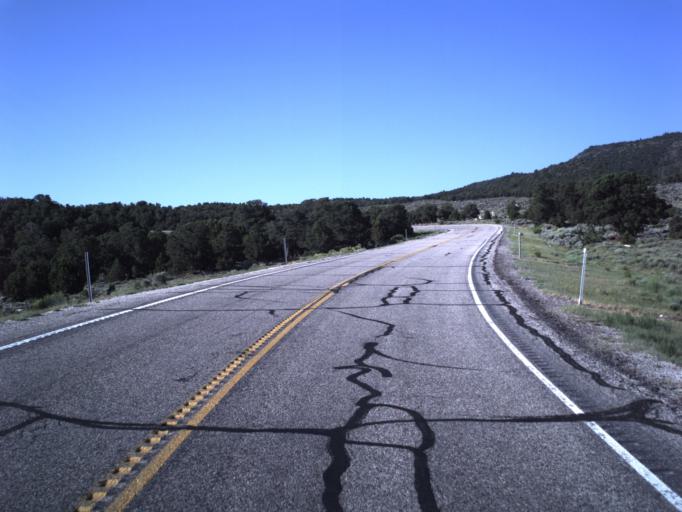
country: US
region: Utah
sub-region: Wayne County
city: Loa
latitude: 38.7060
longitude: -111.4015
